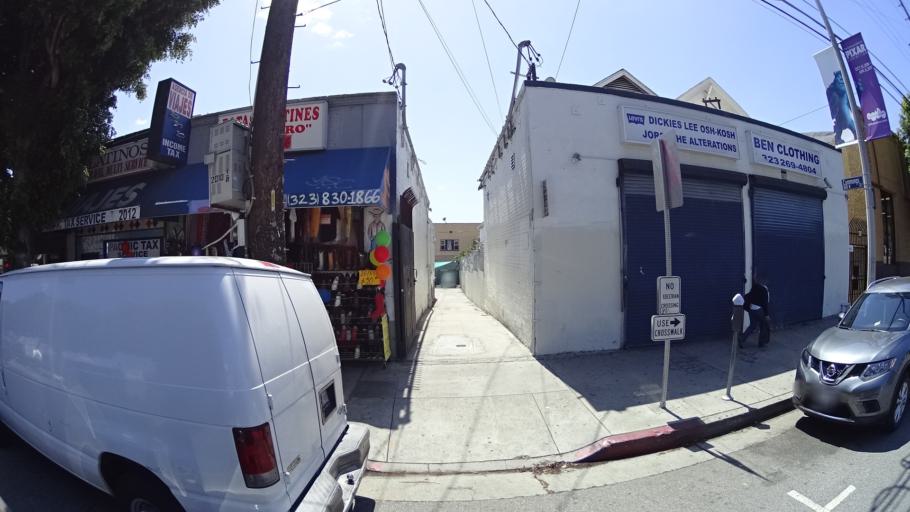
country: US
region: California
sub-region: Los Angeles County
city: Boyle Heights
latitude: 34.0488
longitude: -118.2124
